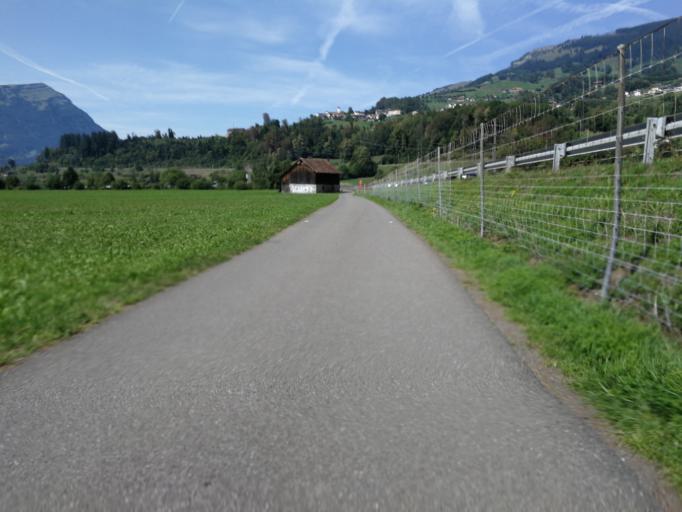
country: CH
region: Schwyz
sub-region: Bezirk Schwyz
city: Steinen
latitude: 47.0457
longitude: 8.5974
